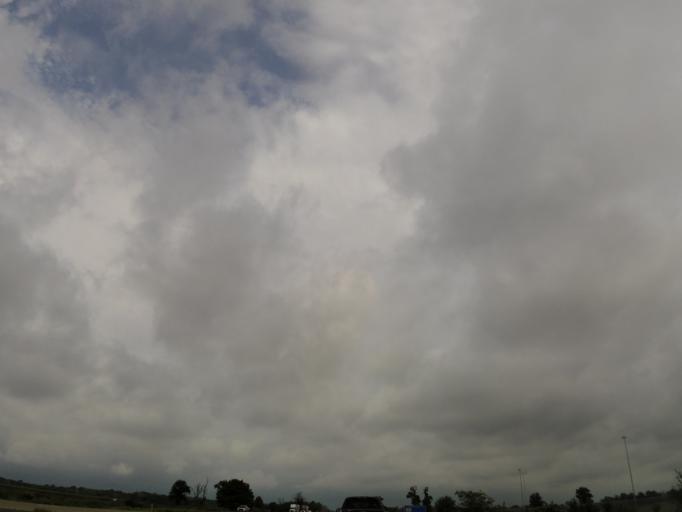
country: US
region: Illinois
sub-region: Jefferson County
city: Ina
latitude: 38.1290
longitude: -88.9118
